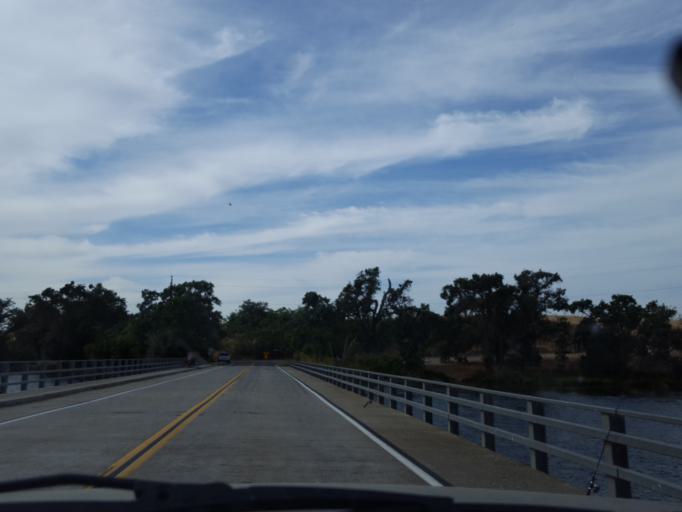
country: US
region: California
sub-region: Merced County
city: Planada
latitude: 37.5239
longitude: -120.3213
